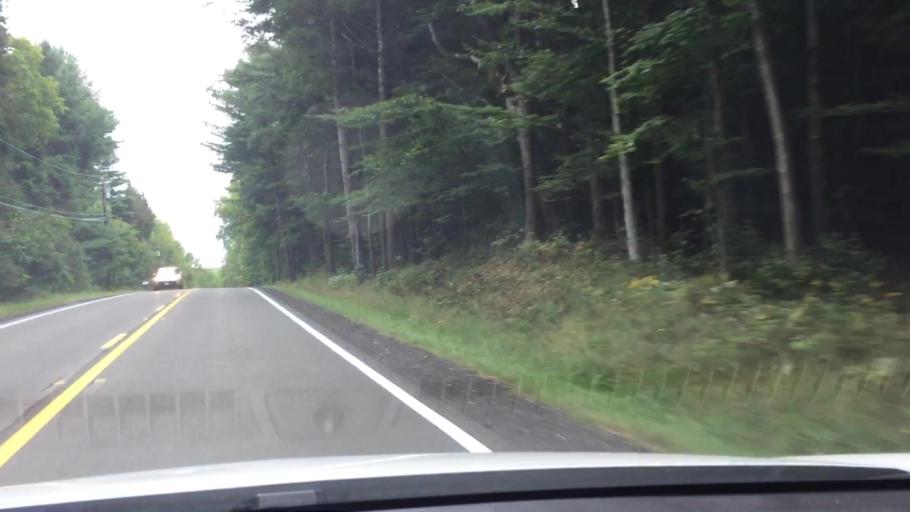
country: US
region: Massachusetts
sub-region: Berkshire County
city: Becket
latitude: 42.3515
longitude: -73.0943
